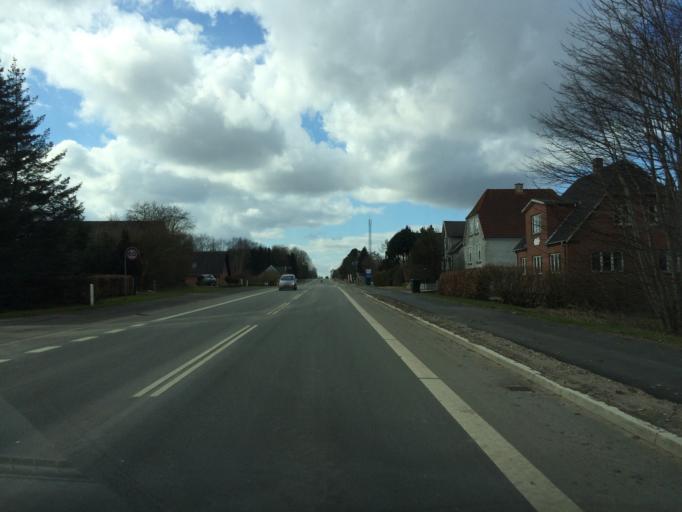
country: DK
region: South Denmark
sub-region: Assens Kommune
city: Tommerup Stationsby
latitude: 55.3874
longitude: 10.1904
